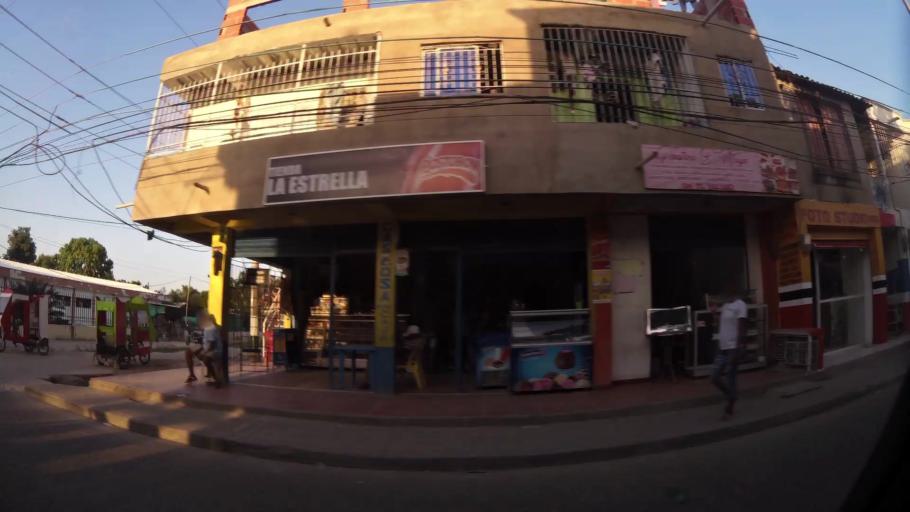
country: CO
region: Bolivar
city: Cartagena
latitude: 10.4082
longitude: -75.4552
